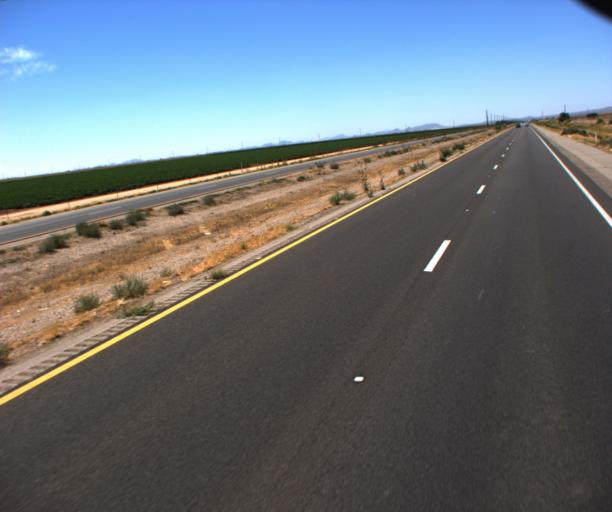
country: US
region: Arizona
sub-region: Pinal County
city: Maricopa
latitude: 32.9922
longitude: -112.0481
